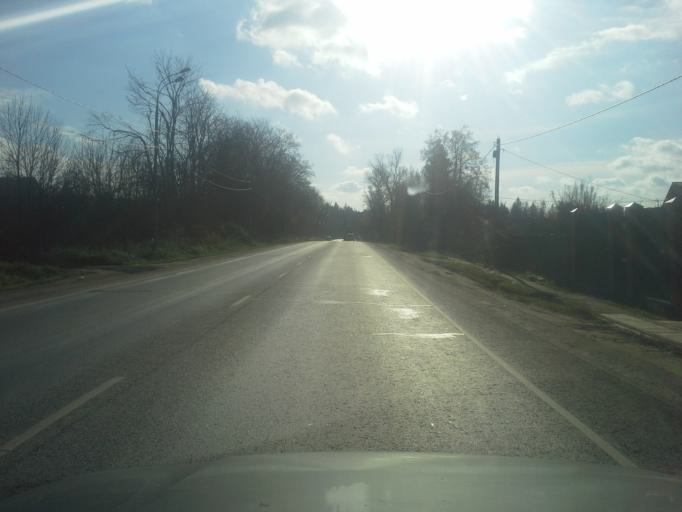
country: RU
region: Moskovskaya
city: Bol'shiye Vyazemy
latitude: 55.6629
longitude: 36.9650
